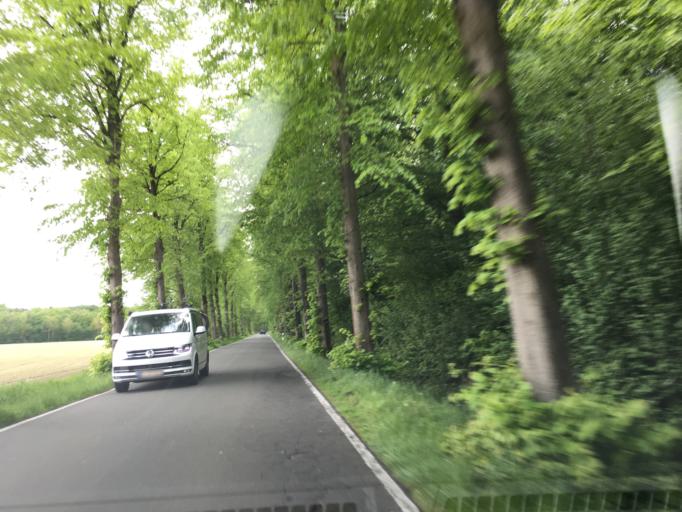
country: DE
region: North Rhine-Westphalia
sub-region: Regierungsbezirk Munster
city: Senden
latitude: 51.9407
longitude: 7.5119
